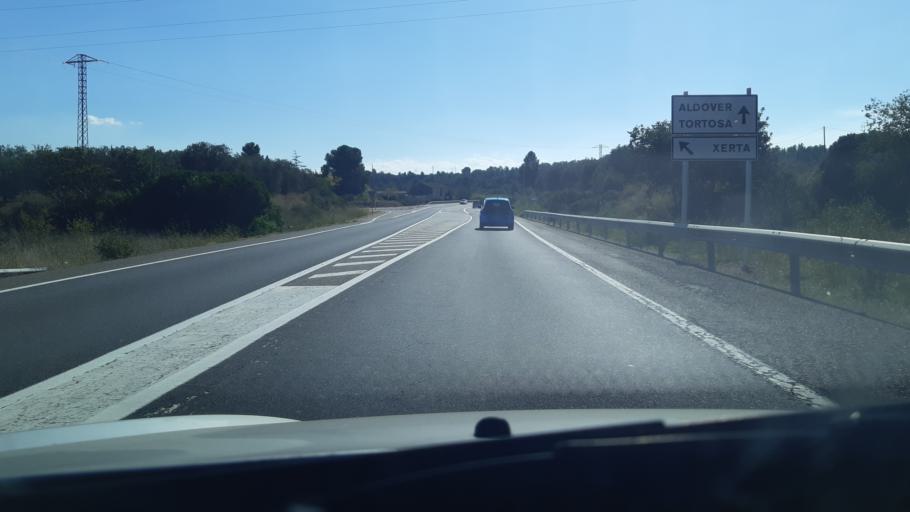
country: ES
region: Catalonia
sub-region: Provincia de Tarragona
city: Tivenys
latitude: 40.9060
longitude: 0.4833
